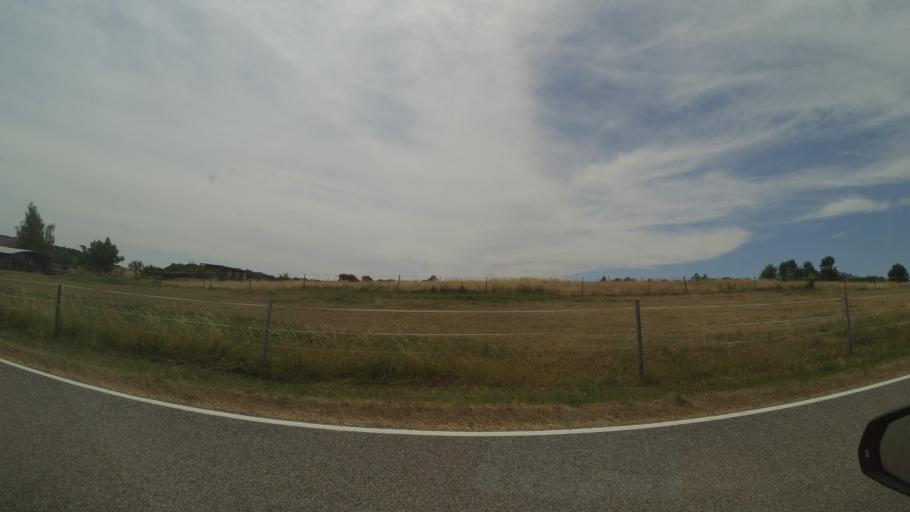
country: DE
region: Saarland
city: Mettlach
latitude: 49.4276
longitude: 6.5553
